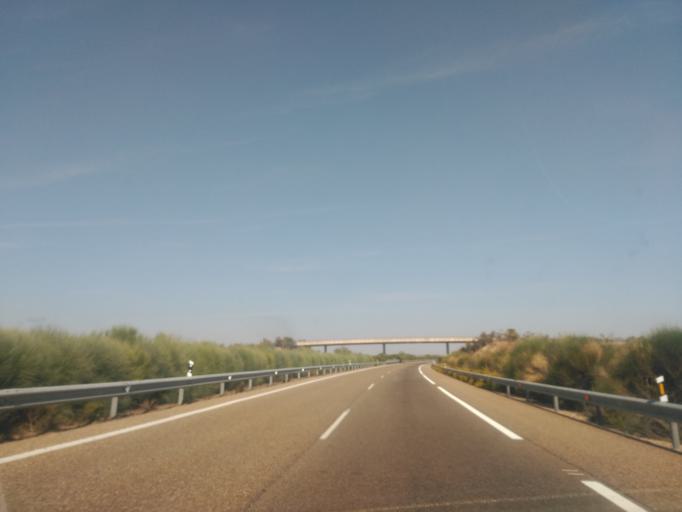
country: ES
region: Castille and Leon
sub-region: Provincia de Zamora
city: Castrillo de la Guarena
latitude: 41.2516
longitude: -5.2890
